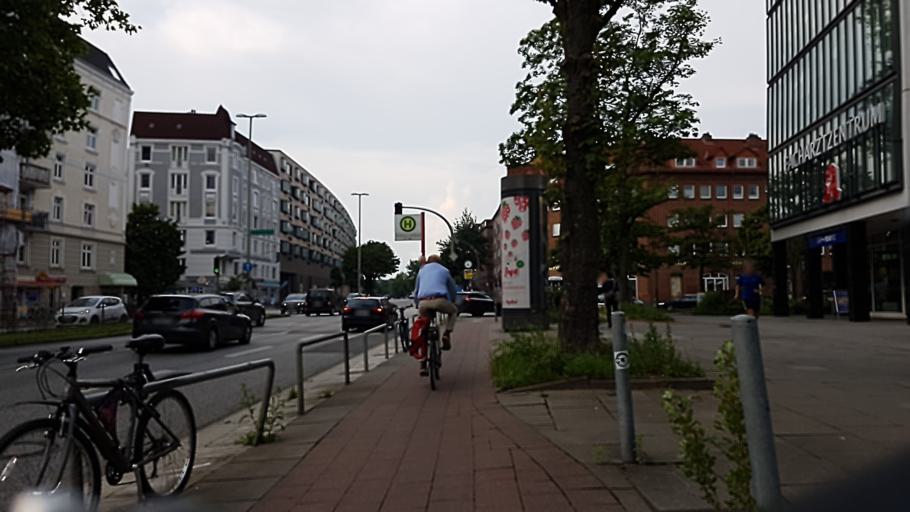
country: DE
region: Hamburg
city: Hamburg
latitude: 53.5832
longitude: 10.0194
